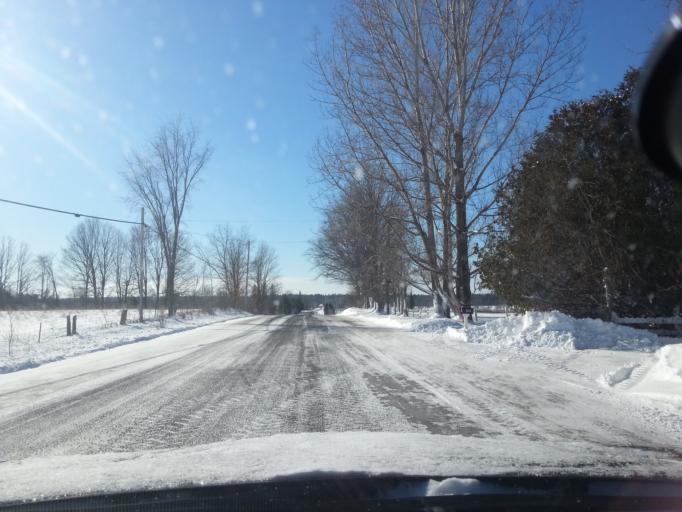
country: CA
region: Ontario
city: Arnprior
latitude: 45.2833
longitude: -76.2981
